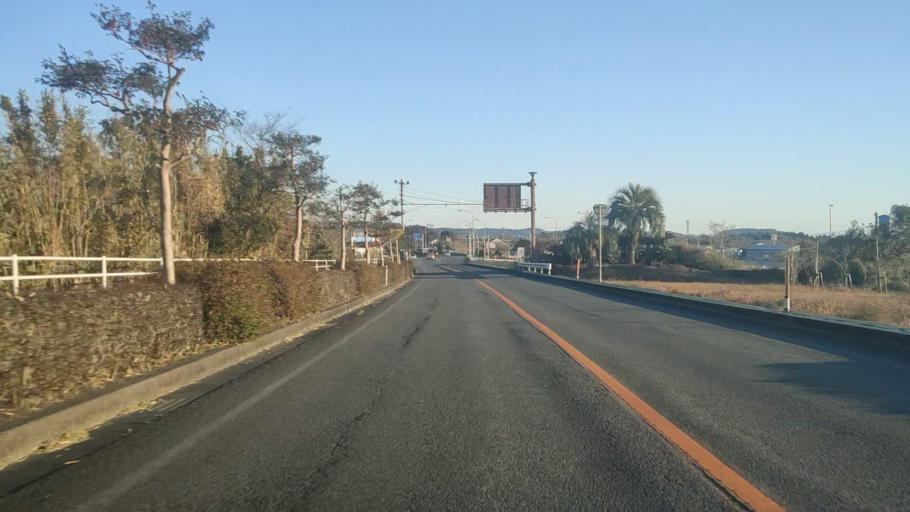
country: JP
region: Miyazaki
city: Tsuma
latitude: 32.0402
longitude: 131.4687
